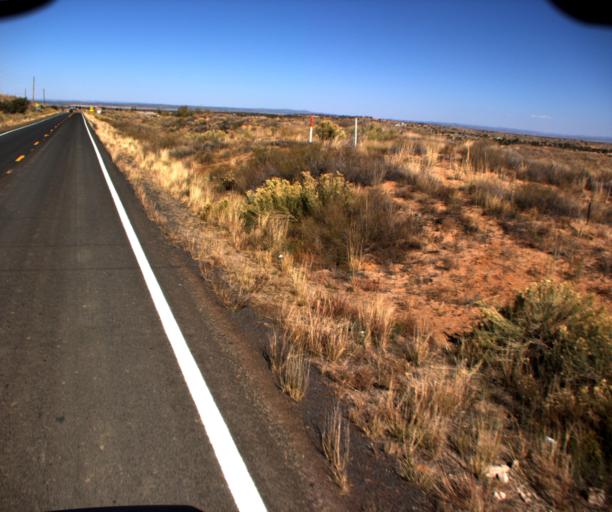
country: US
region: Arizona
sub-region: Navajo County
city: First Mesa
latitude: 35.9147
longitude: -110.6640
